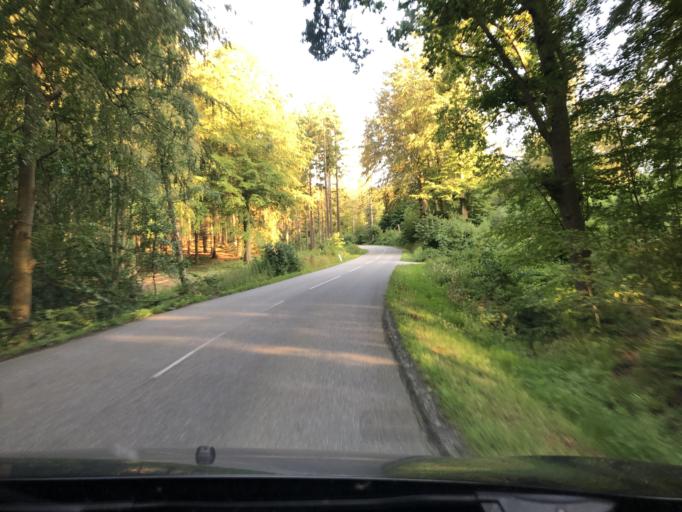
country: DK
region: South Denmark
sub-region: Vejle Kommune
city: Borkop
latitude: 55.6911
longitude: 9.6178
